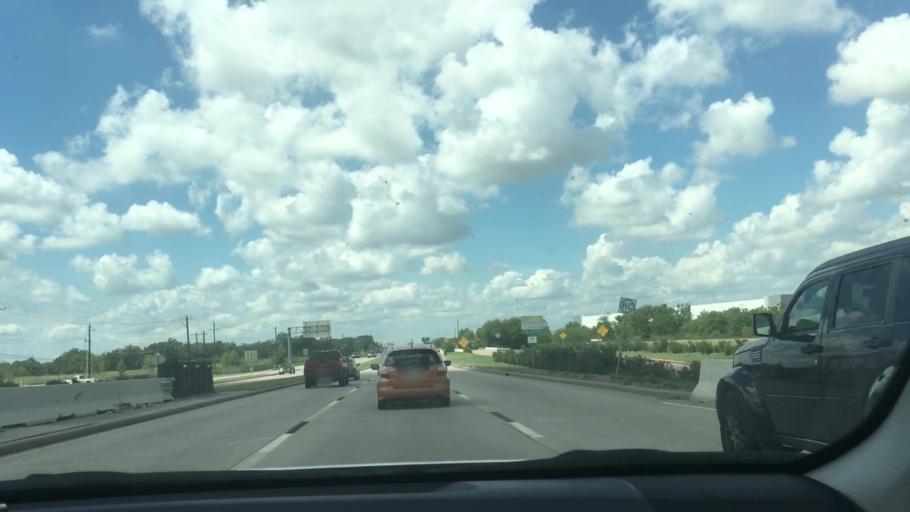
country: US
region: Texas
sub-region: Fort Bend County
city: Missouri City
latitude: 29.6259
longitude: -95.5194
